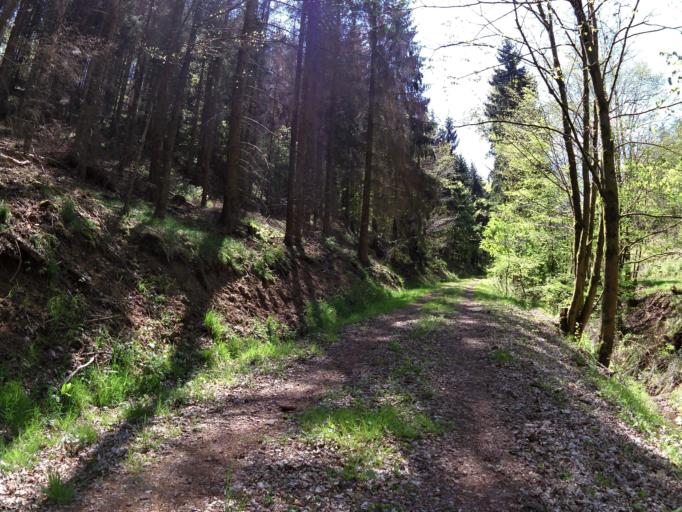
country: DE
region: Thuringia
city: Wolfsburg-Unkeroda
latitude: 50.9676
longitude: 10.2635
